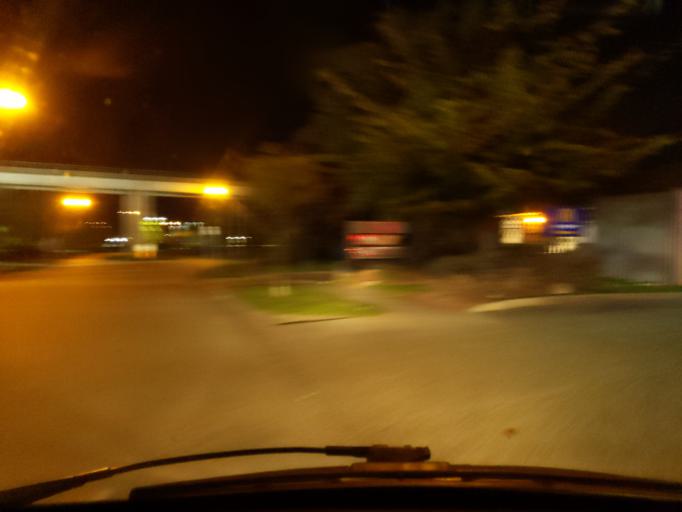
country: CA
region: British Columbia
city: New Westminster
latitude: 49.2030
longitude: -122.8800
